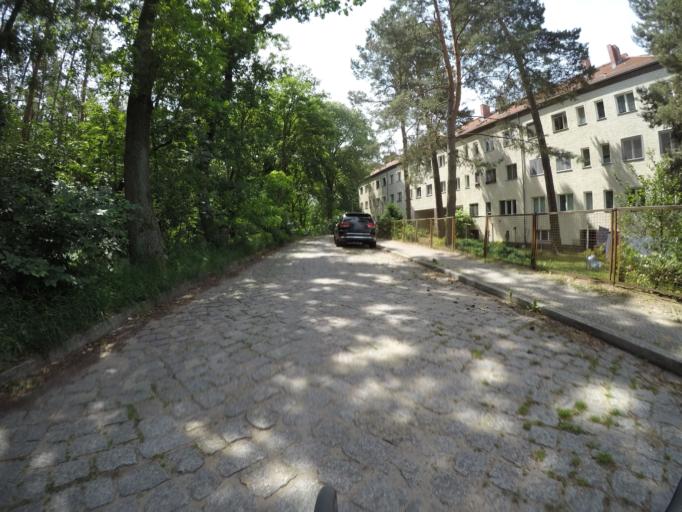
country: DE
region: Berlin
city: Berlin Koepenick
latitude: 52.4639
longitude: 13.5966
